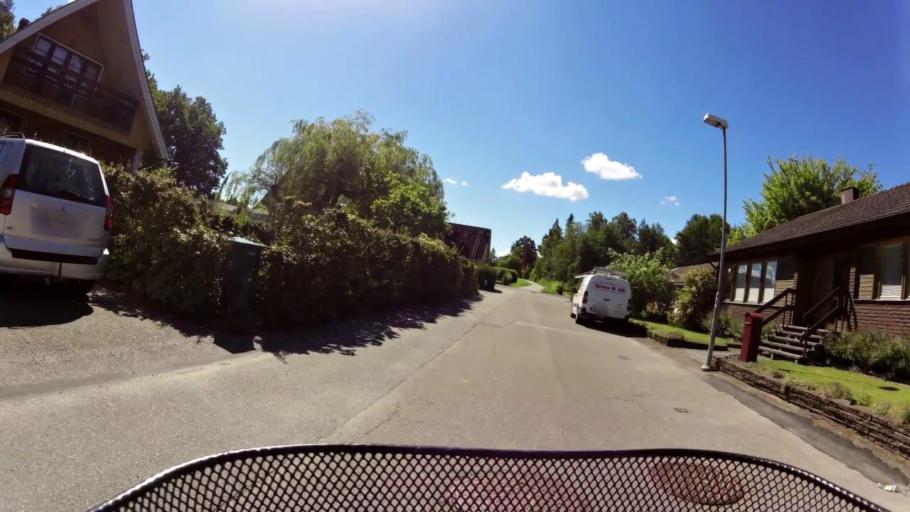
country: SE
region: OEstergoetland
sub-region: Linkopings Kommun
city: Sturefors
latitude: 58.3887
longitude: 15.6985
